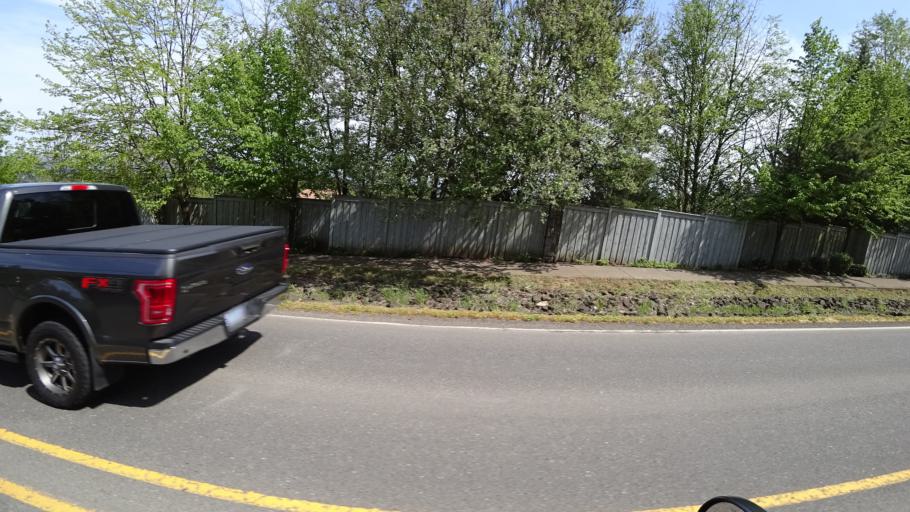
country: US
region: Oregon
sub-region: Washington County
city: Aloha
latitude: 45.4563
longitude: -122.8569
